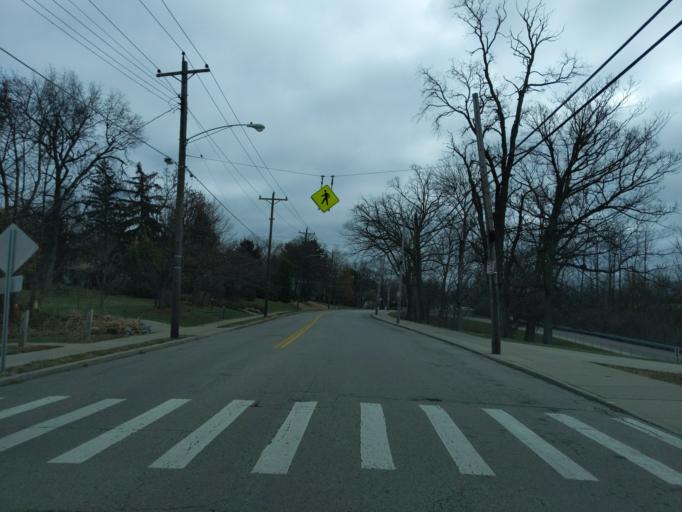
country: US
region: Ohio
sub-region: Hamilton County
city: North College Hill
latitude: 39.1930
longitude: -84.5493
